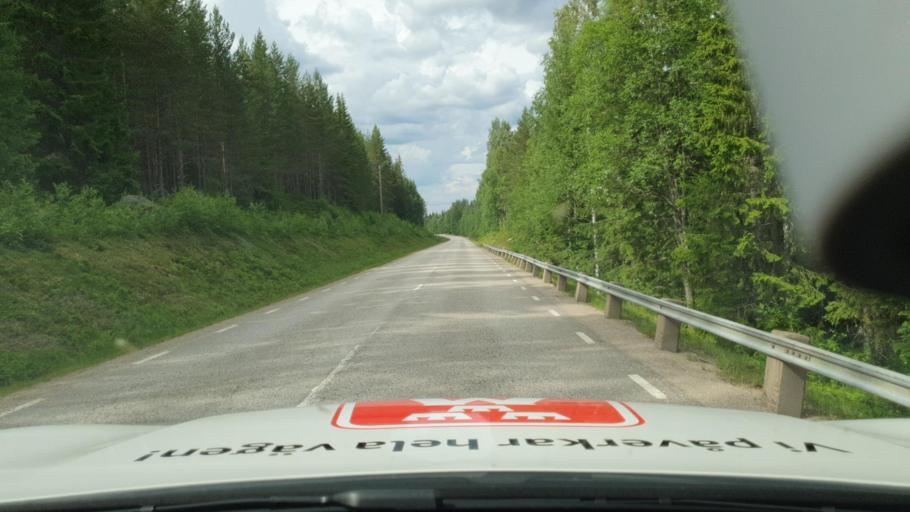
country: NO
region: Hedmark
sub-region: Trysil
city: Innbygda
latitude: 61.0048
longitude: 12.4844
